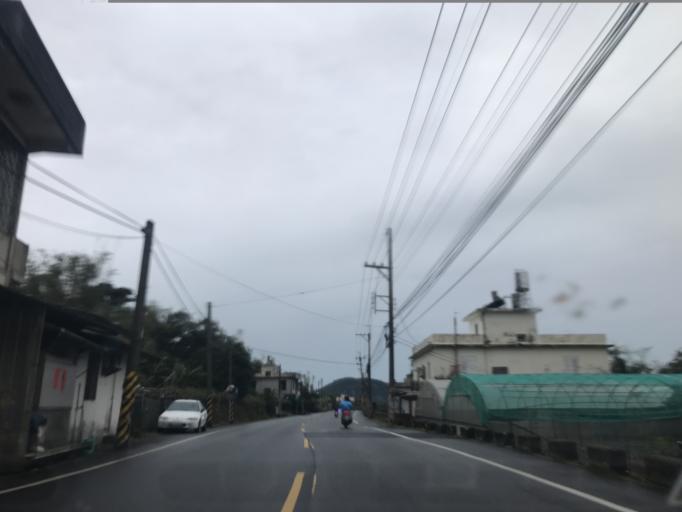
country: TW
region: Taiwan
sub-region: Hsinchu
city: Zhubei
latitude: 24.8407
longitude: 121.1211
